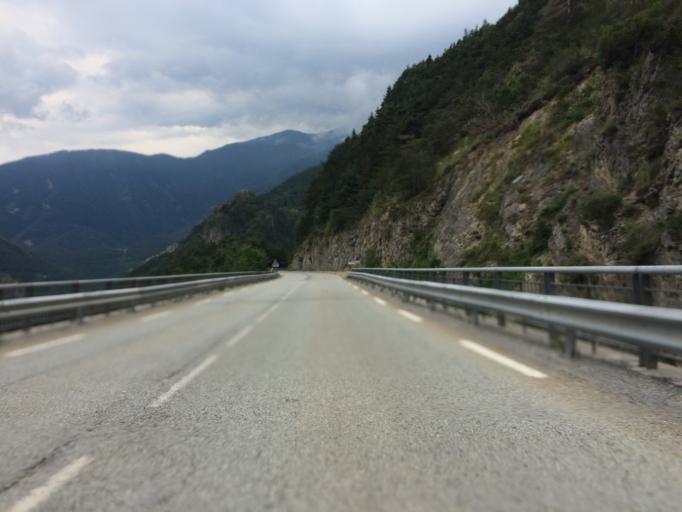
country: FR
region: Provence-Alpes-Cote d'Azur
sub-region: Departement des Alpes-Maritimes
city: Tende
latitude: 44.1334
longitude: 7.5672
